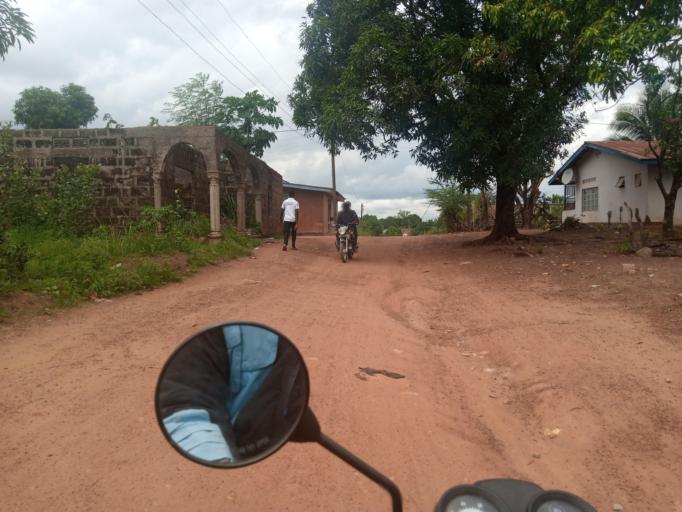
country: SL
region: Southern Province
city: Bo
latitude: 7.9505
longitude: -11.7532
